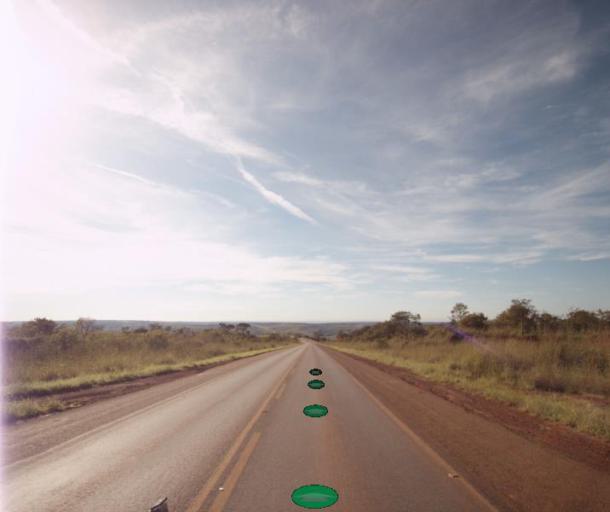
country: BR
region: Federal District
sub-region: Brasilia
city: Brasilia
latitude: -15.7401
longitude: -48.3847
